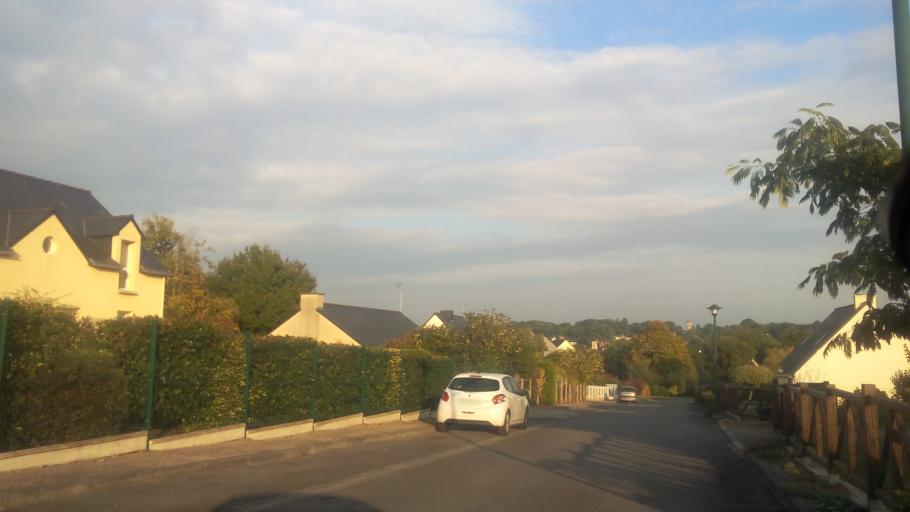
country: FR
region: Brittany
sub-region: Departement du Morbihan
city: Saint-Jean-la-Poterie
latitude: 47.6357
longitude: -2.1312
